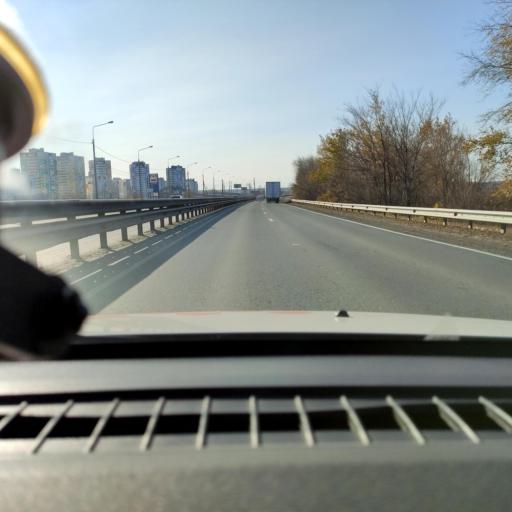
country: RU
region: Samara
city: Samara
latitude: 53.1016
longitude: 50.1617
